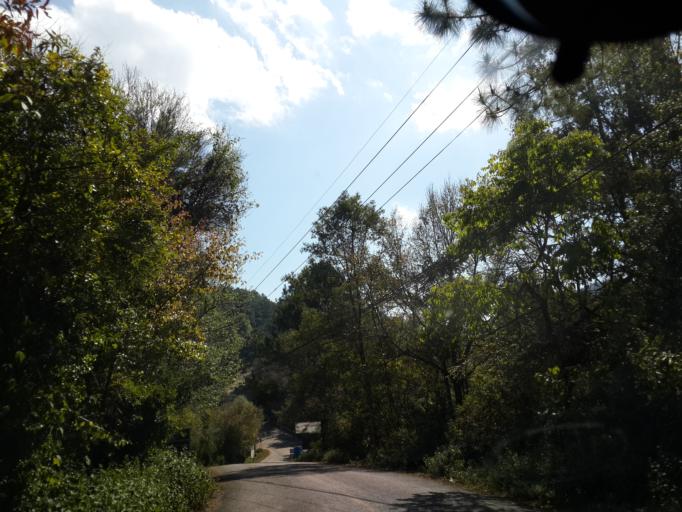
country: TH
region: Chiang Mai
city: Fang
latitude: 19.8983
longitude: 99.0457
